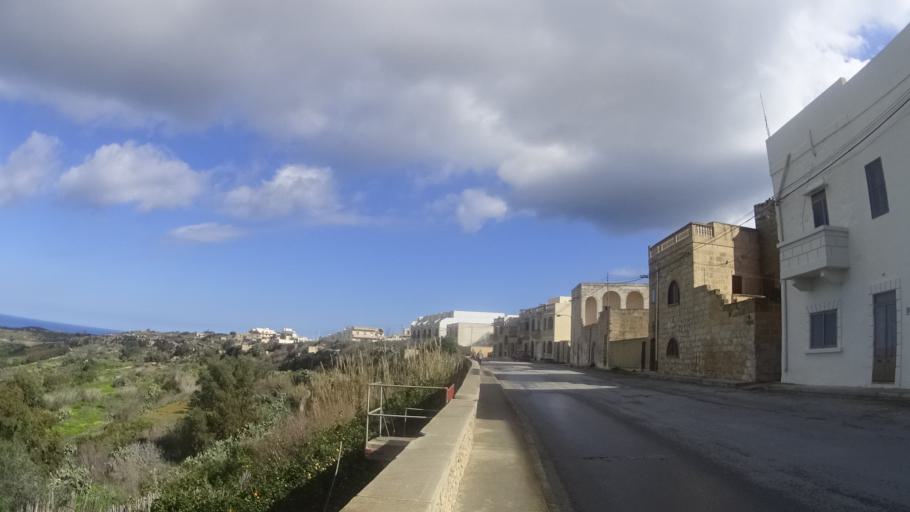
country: MT
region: In-Nadur
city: Nadur
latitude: 36.0433
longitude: 14.2904
